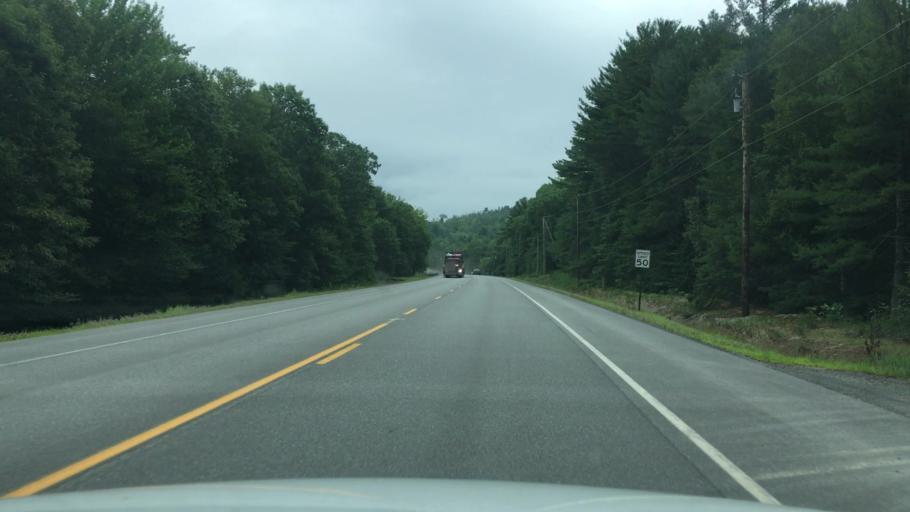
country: US
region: Maine
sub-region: Penobscot County
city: Bradley
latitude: 44.8243
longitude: -68.4846
